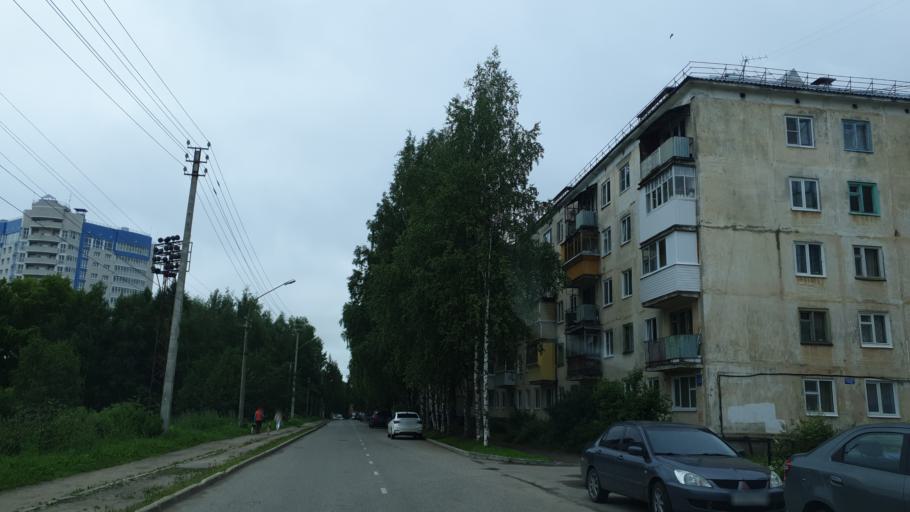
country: RU
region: Komi Republic
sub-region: Syktyvdinskiy Rayon
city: Syktyvkar
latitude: 61.6626
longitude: 50.8245
